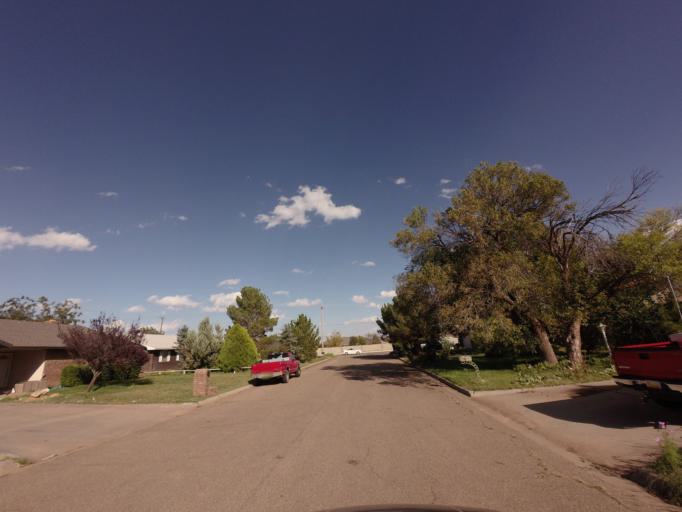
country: US
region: New Mexico
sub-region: Curry County
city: Clovis
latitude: 34.4379
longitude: -103.1793
